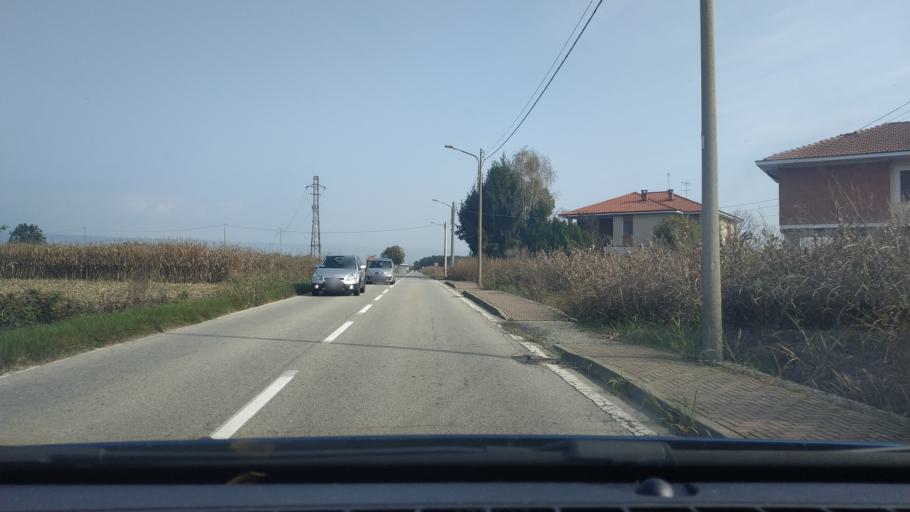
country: IT
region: Piedmont
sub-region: Provincia di Torino
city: Romano Canavese
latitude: 45.4055
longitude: 7.8731
